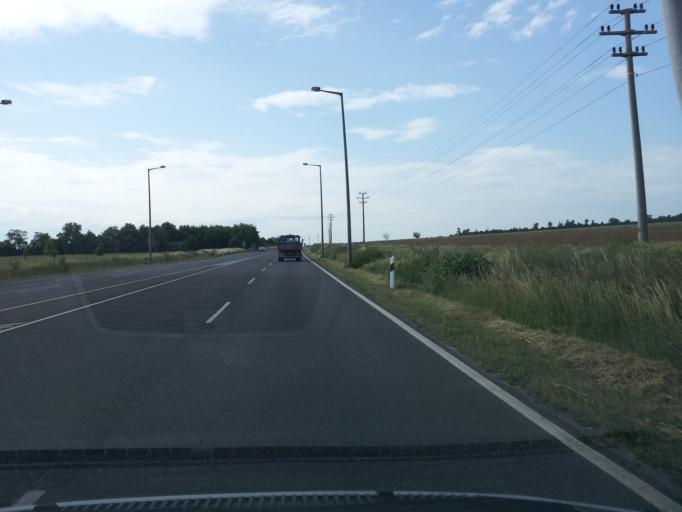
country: HU
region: Veszprem
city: Veszprem
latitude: 47.0715
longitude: 17.9194
